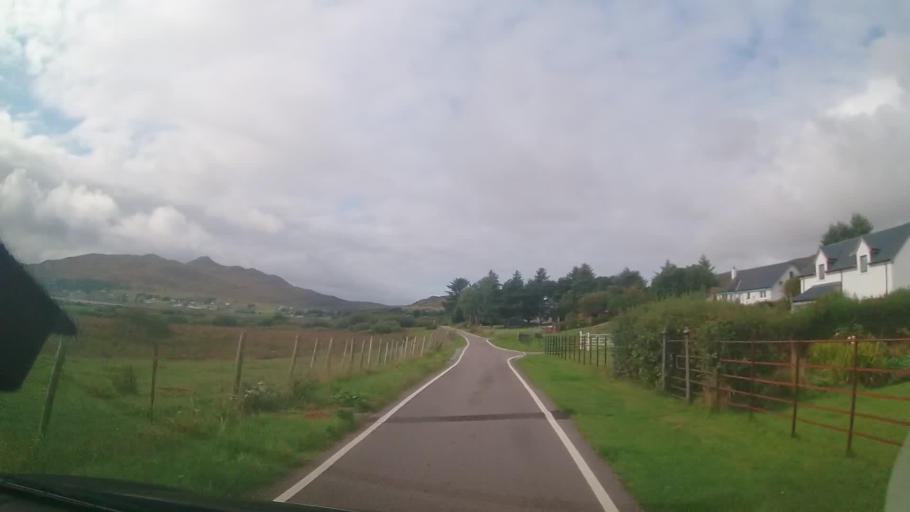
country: GB
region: Scotland
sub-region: Argyll and Bute
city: Isle Of Mull
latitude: 56.6940
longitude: -6.0964
